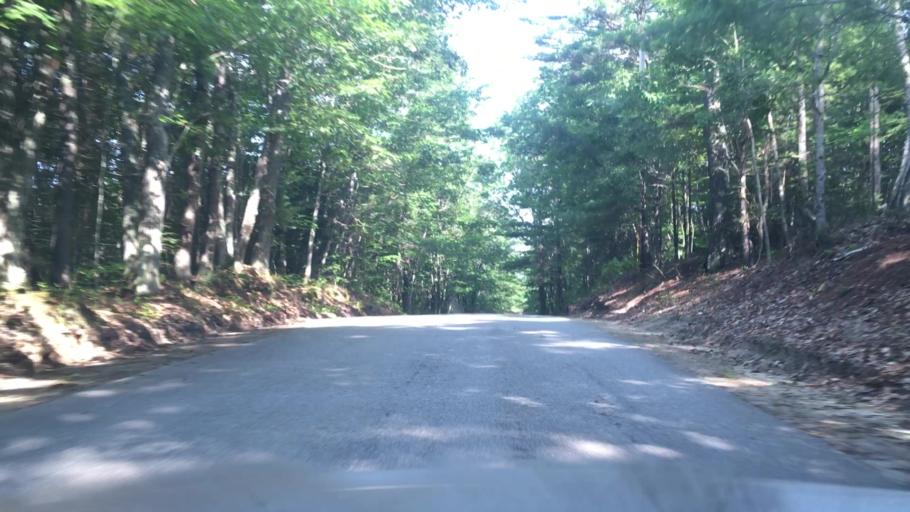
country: US
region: Maine
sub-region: Kennebec County
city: Monmouth
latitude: 44.2376
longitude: -70.0745
